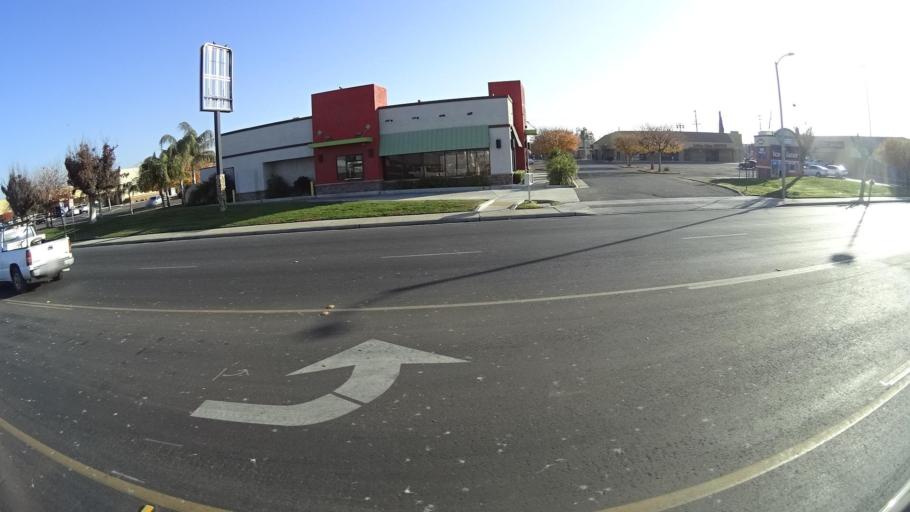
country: US
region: California
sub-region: Kern County
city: Delano
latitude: 35.7769
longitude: -119.2495
